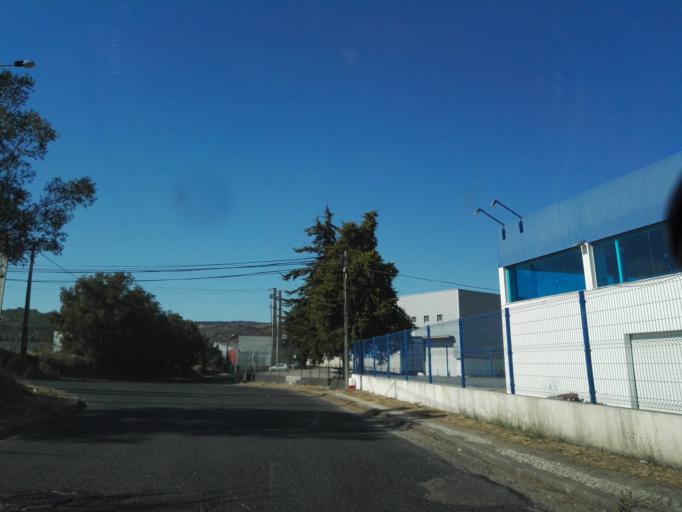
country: PT
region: Lisbon
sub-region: Vila Franca de Xira
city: Sobralinho
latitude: 38.9055
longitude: -9.0262
